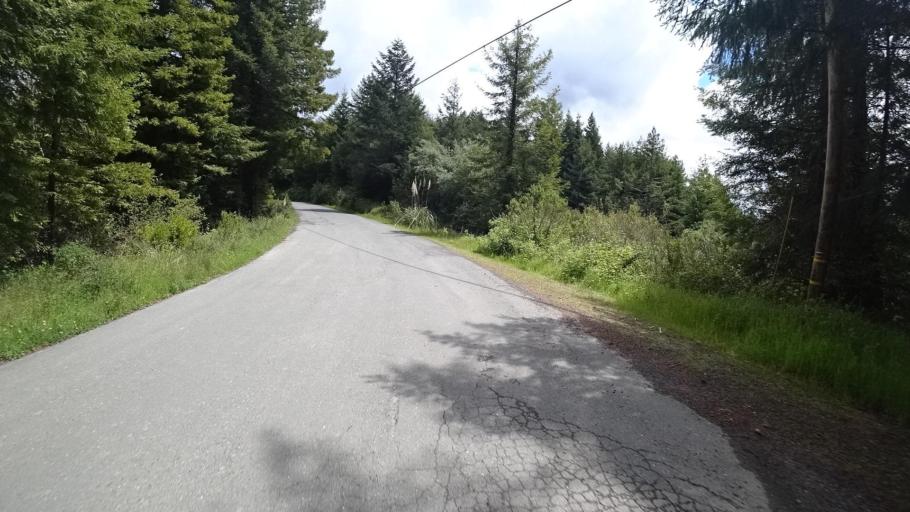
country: US
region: California
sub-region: Humboldt County
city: Blue Lake
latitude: 40.8016
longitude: -123.8795
